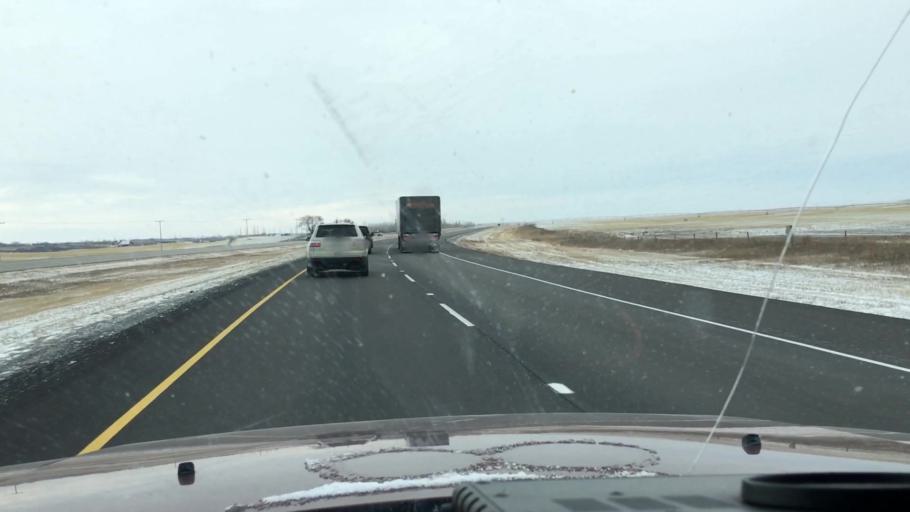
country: CA
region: Saskatchewan
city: Saskatoon
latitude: 51.7797
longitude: -106.4767
